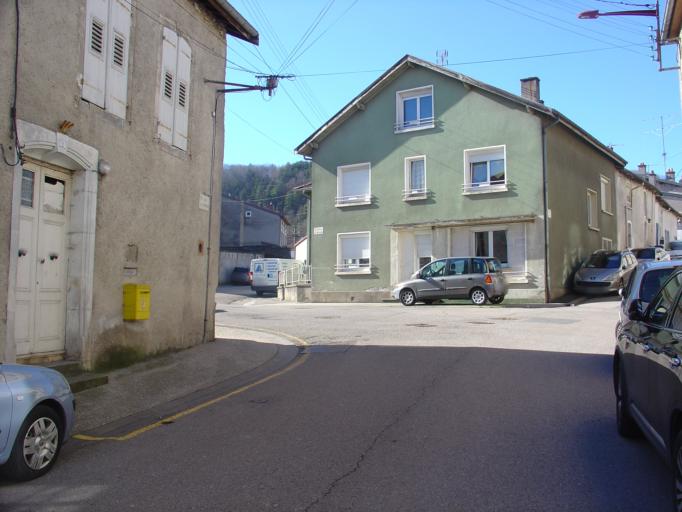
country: FR
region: Lorraine
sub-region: Departement de Meurthe-et-Moselle
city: Blenod-les-Toul
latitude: 48.5993
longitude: 5.8324
